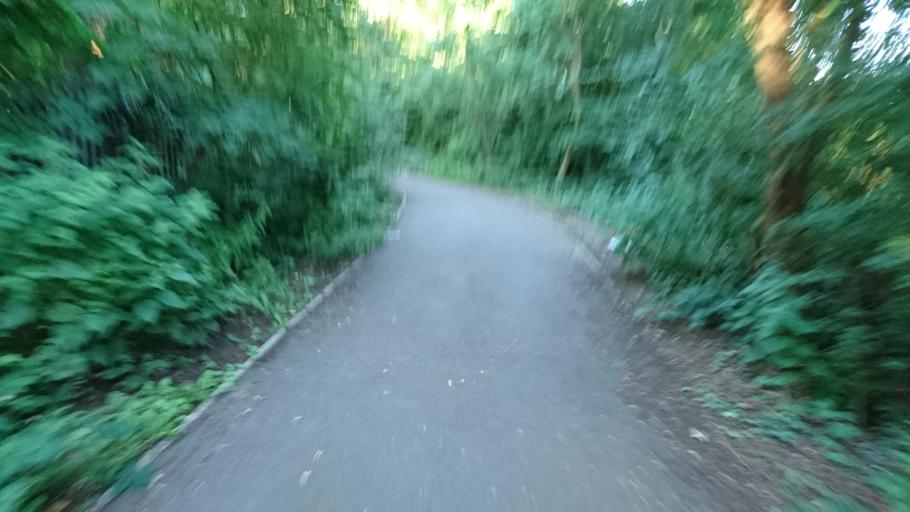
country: GB
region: England
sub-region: Greater London
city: Hendon
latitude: 51.6065
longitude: -0.2014
